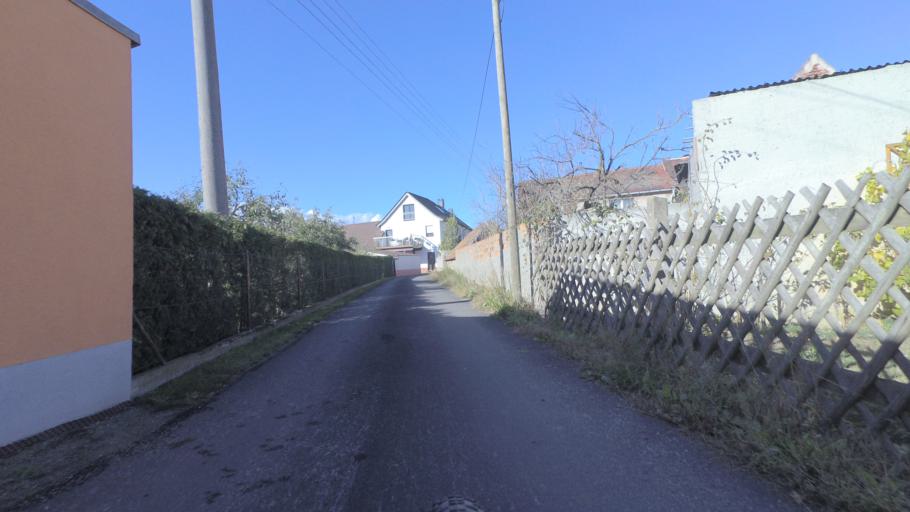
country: DE
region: Saxony
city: Nauwalde
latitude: 51.4433
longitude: 13.3730
